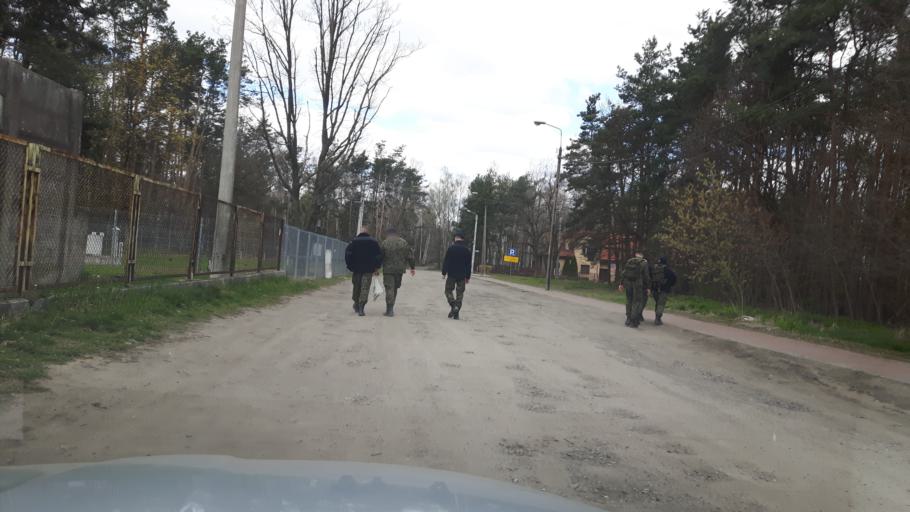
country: PL
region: Masovian Voivodeship
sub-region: Powiat wolominski
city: Wolomin
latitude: 52.3479
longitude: 21.2221
